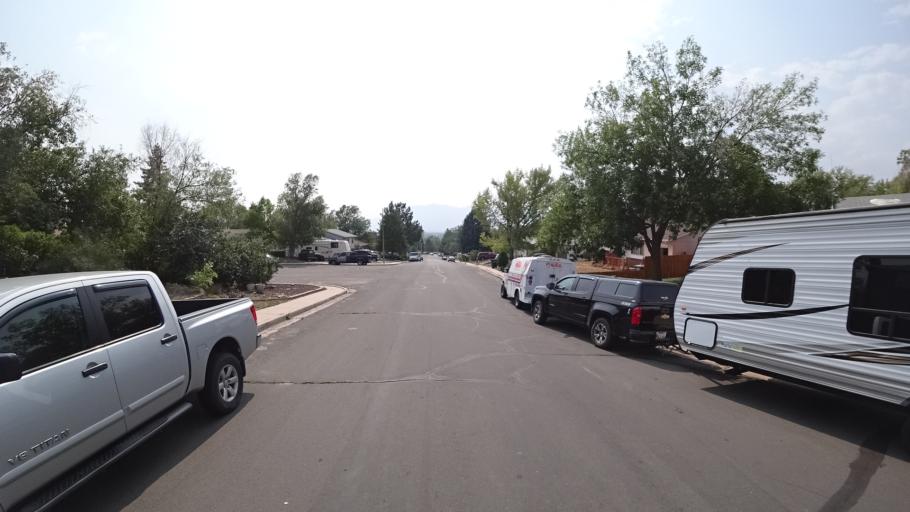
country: US
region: Colorado
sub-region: El Paso County
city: Cimarron Hills
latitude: 38.8313
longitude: -104.7497
